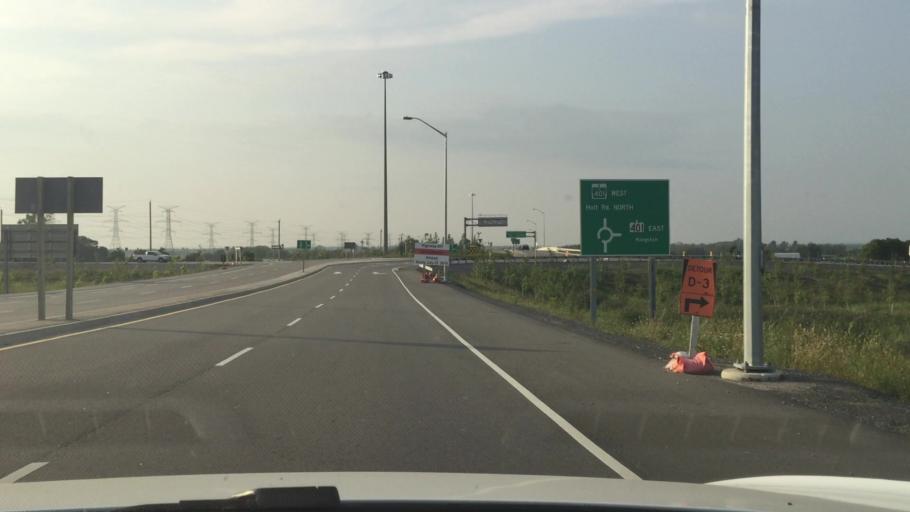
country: CA
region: Ontario
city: Oshawa
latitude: 43.8818
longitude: -78.7212
